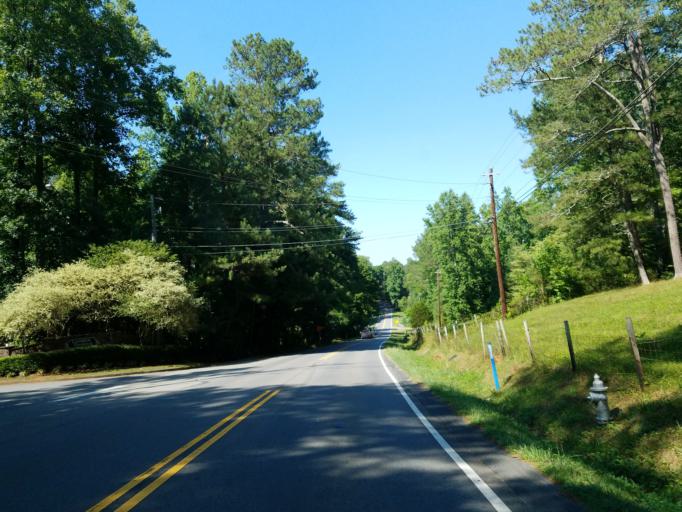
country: US
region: Georgia
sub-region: Fulton County
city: Milton
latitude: 34.1103
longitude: -84.3411
